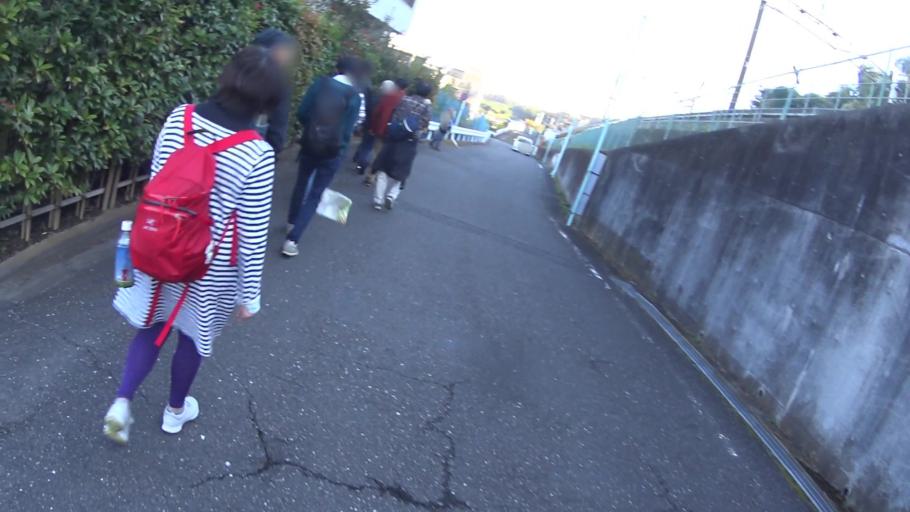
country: JP
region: Tokyo
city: Chofugaoka
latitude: 35.6359
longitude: 139.5044
